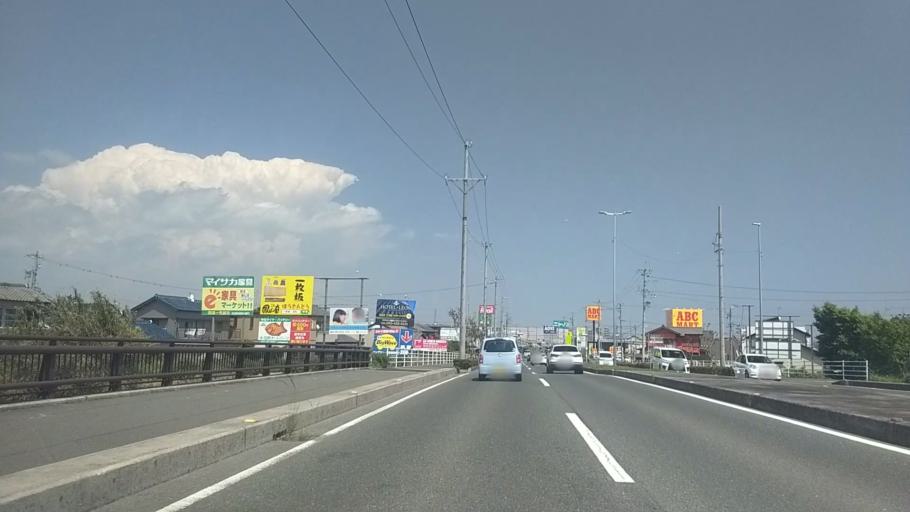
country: JP
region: Shizuoka
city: Hamamatsu
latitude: 34.6989
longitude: 137.6676
